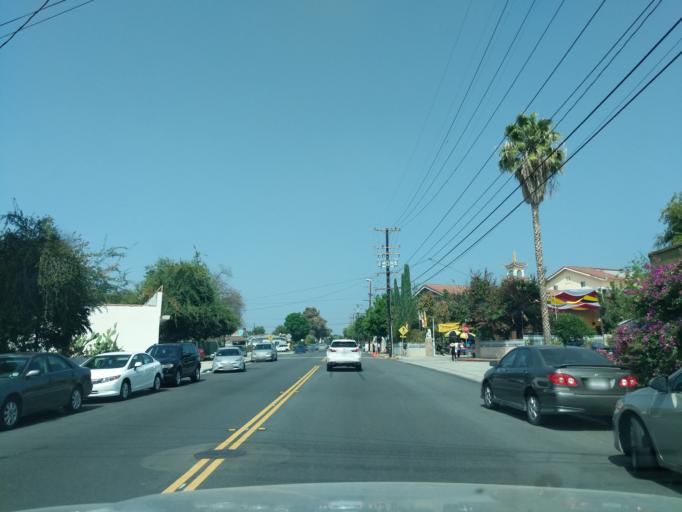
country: US
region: California
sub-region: Los Angeles County
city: East San Gabriel
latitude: 34.0929
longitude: -118.0961
